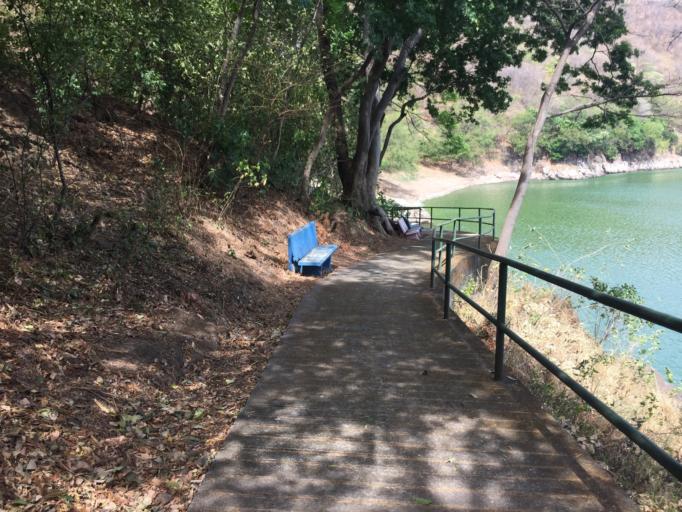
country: NI
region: Managua
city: Managua
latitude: 12.1376
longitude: -86.2710
